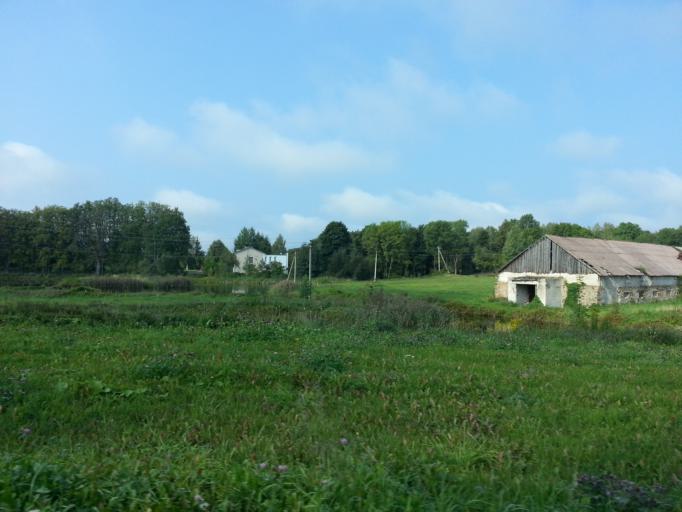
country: LT
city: Grigiskes
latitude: 54.7643
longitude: 25.0455
